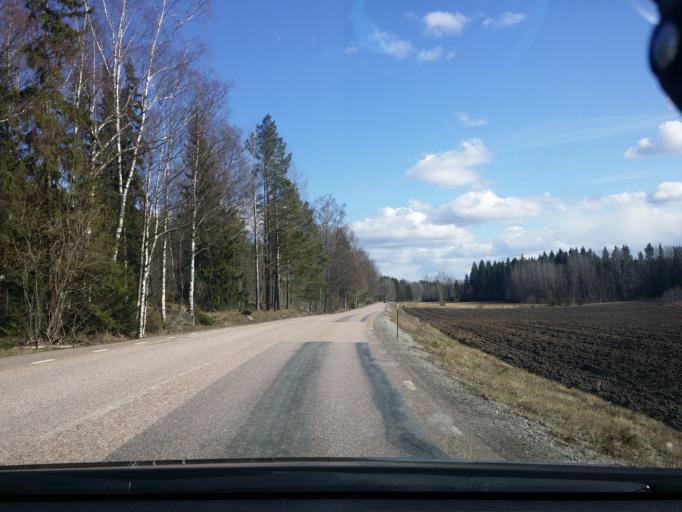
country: SE
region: Vaestmanland
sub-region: Sala Kommun
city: Sala
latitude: 59.9841
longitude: 16.4835
